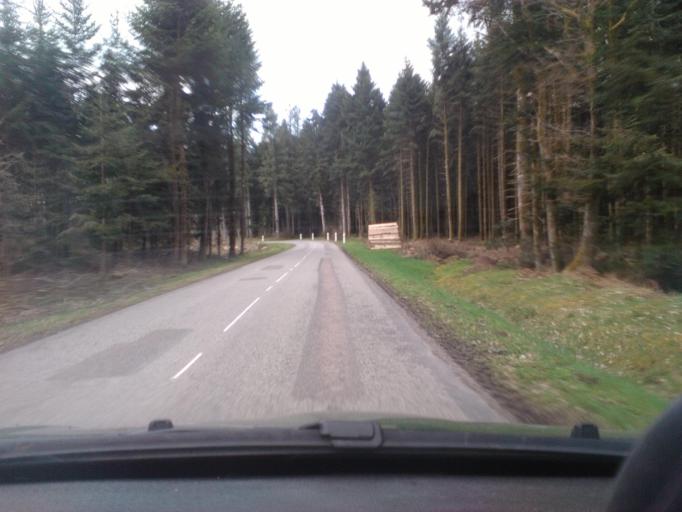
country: FR
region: Lorraine
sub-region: Departement des Vosges
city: Etival-Clairefontaine
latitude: 48.3335
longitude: 6.8231
